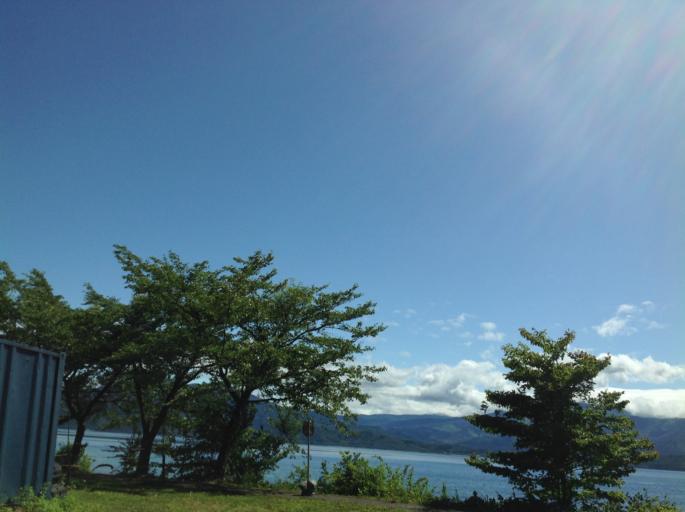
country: JP
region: Akita
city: Kakunodatemachi
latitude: 39.7114
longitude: 140.6344
